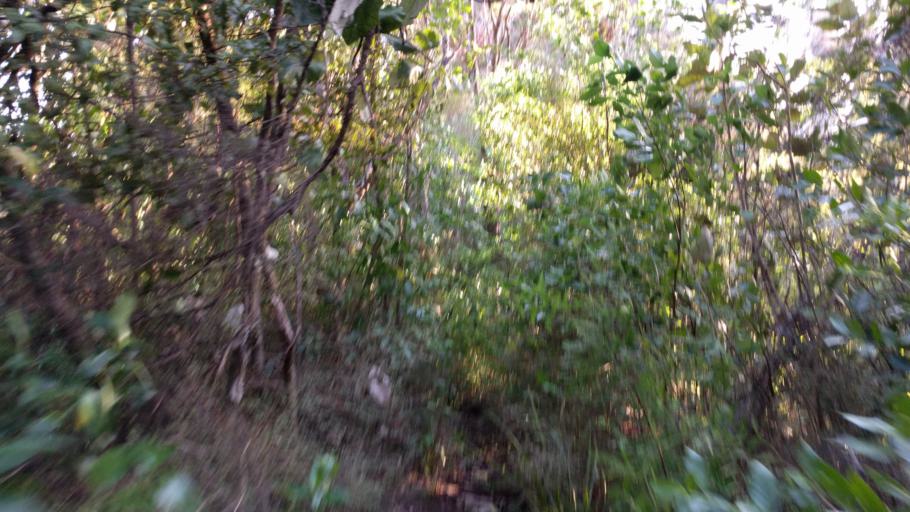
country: NZ
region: Waikato
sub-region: Thames-Coromandel District
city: Thames
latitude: -37.1130
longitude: 175.5274
